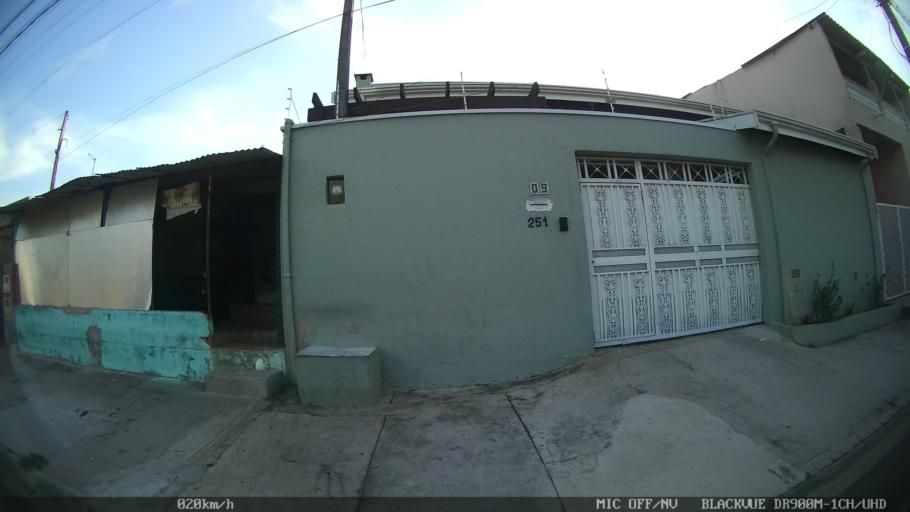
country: BR
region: Sao Paulo
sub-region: Campinas
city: Campinas
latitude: -22.9867
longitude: -47.1170
